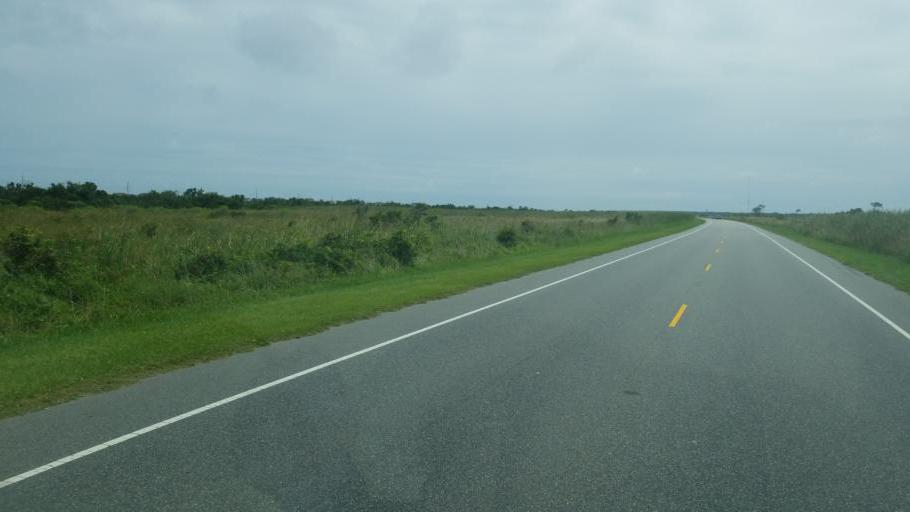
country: US
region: North Carolina
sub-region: Dare County
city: Wanchese
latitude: 35.8622
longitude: -75.5777
